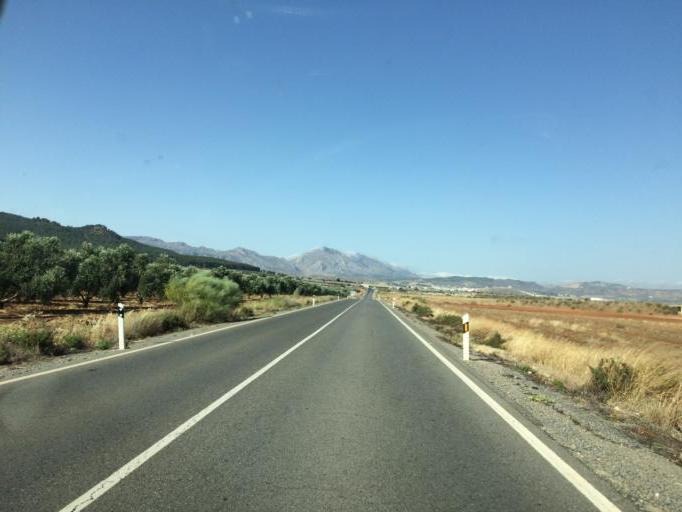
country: ES
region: Andalusia
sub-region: Provincia de Malaga
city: Antequera
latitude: 37.0516
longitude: -4.5020
